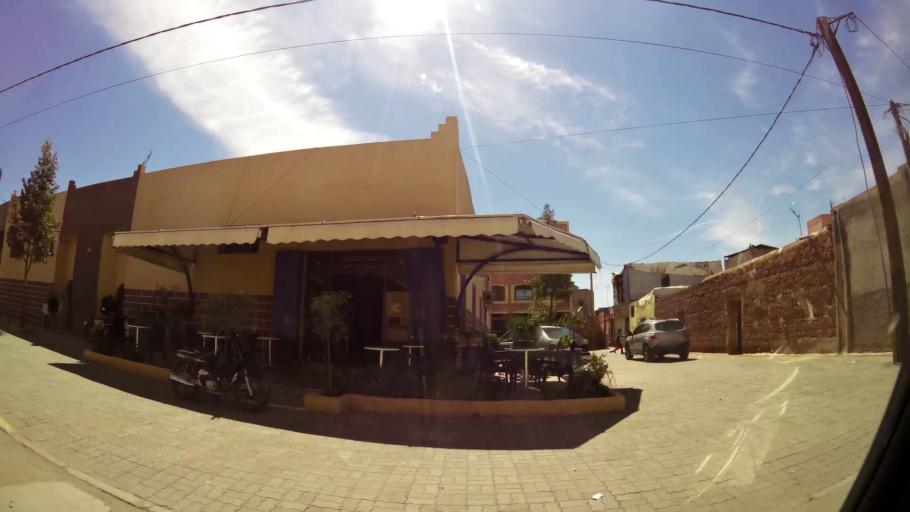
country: MA
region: Marrakech-Tensift-Al Haouz
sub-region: Marrakech
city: Marrakesh
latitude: 31.5976
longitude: -7.9603
